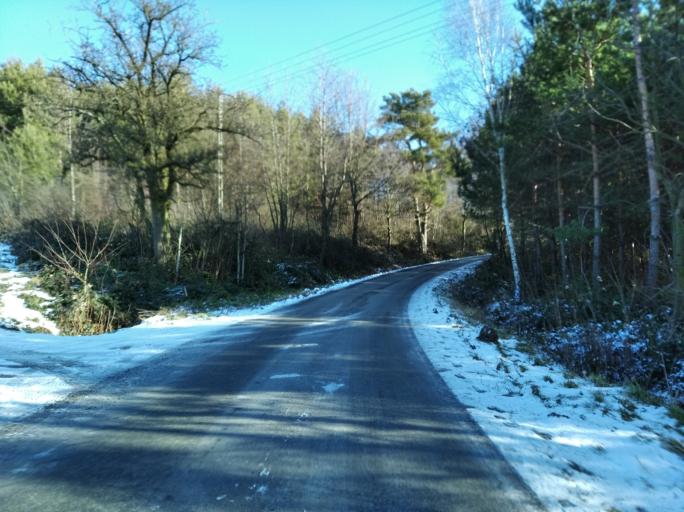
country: PL
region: Subcarpathian Voivodeship
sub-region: Powiat strzyzowski
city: Konieczkowa
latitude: 49.8602
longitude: 21.9515
